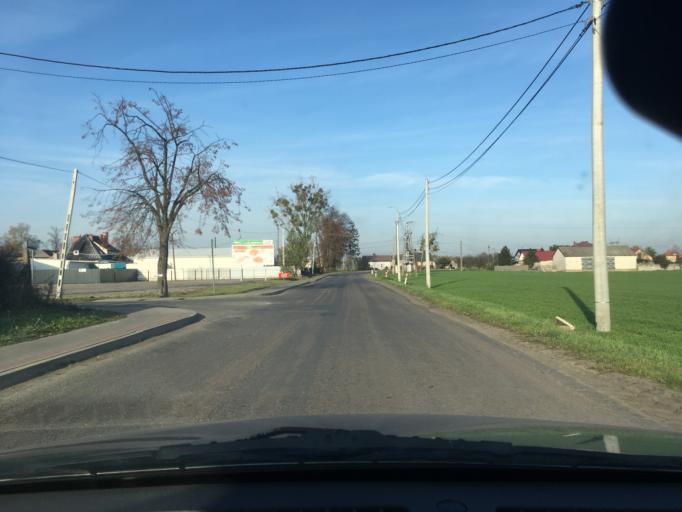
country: PL
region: Masovian Voivodeship
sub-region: Powiat plocki
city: Mala Wies
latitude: 52.4617
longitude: 20.1088
